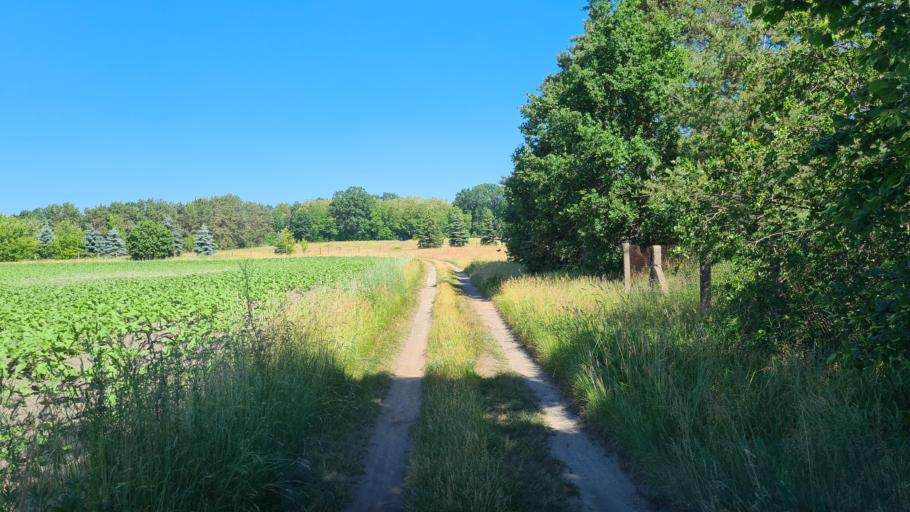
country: DE
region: Brandenburg
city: Plessa
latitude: 51.4693
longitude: 13.6437
